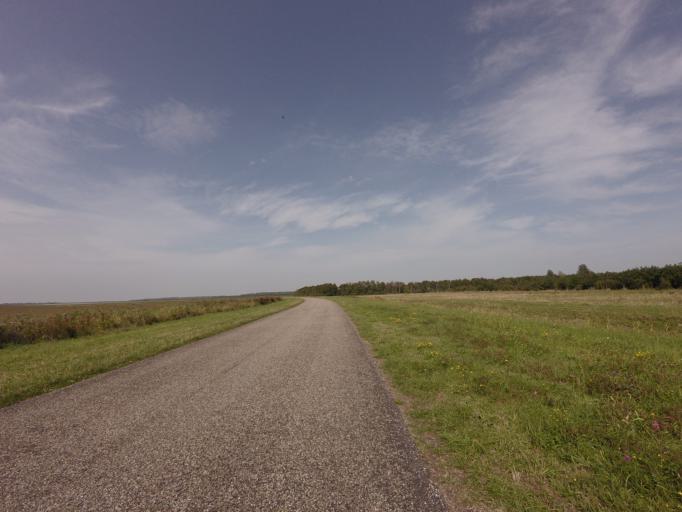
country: NL
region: Groningen
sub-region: Gemeente De Marne
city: Ulrum
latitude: 53.3548
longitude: 6.2647
